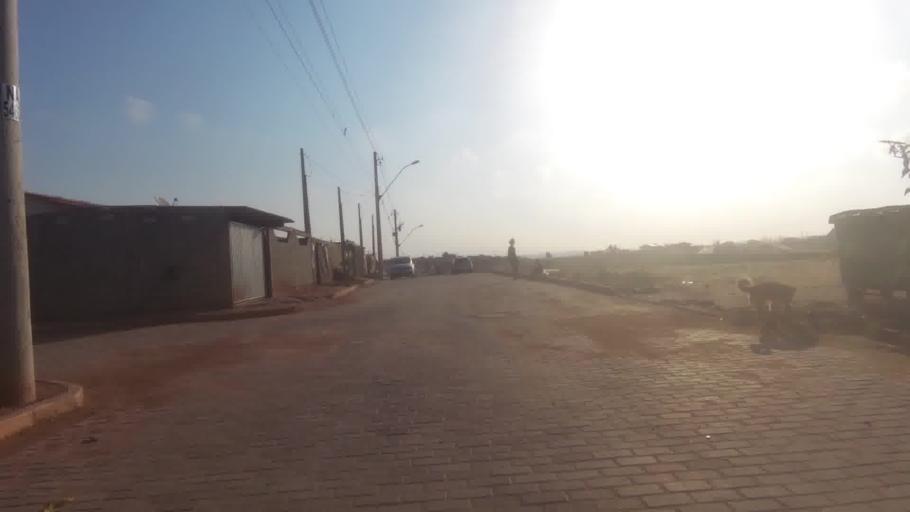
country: BR
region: Espirito Santo
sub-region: Itapemirim
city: Itapemirim
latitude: -21.0183
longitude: -40.8309
